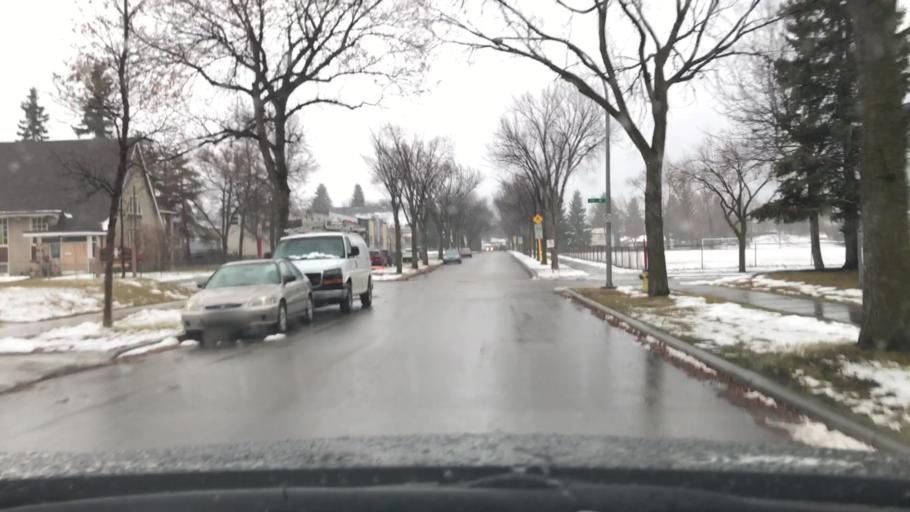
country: CA
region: Alberta
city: Edmonton
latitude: 53.5155
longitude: -113.4584
